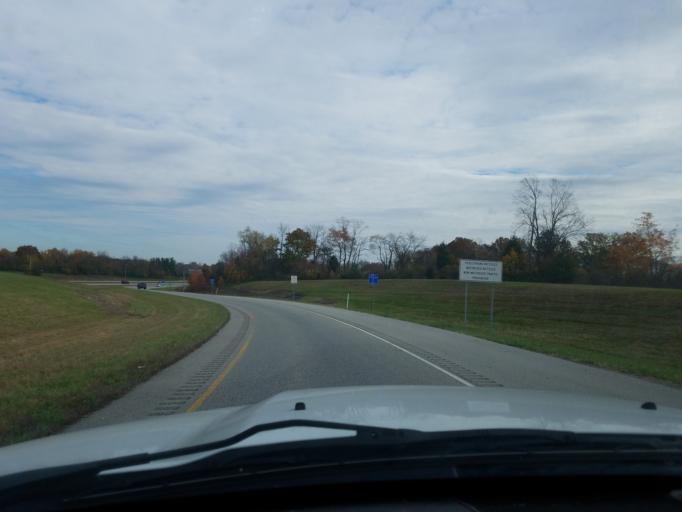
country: US
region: Indiana
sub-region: Clark County
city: Clarksville
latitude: 38.3424
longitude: -85.7985
